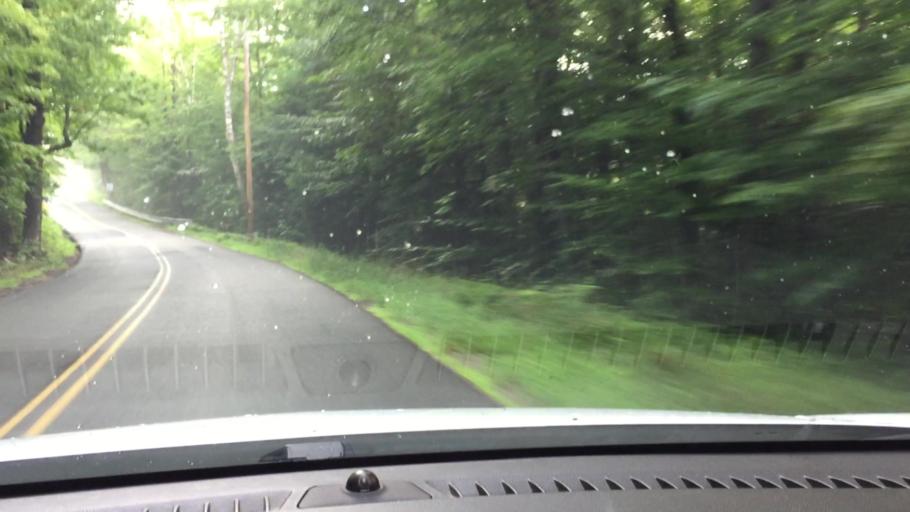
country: US
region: Massachusetts
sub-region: Berkshire County
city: Becket
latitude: 42.4169
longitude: -72.9828
